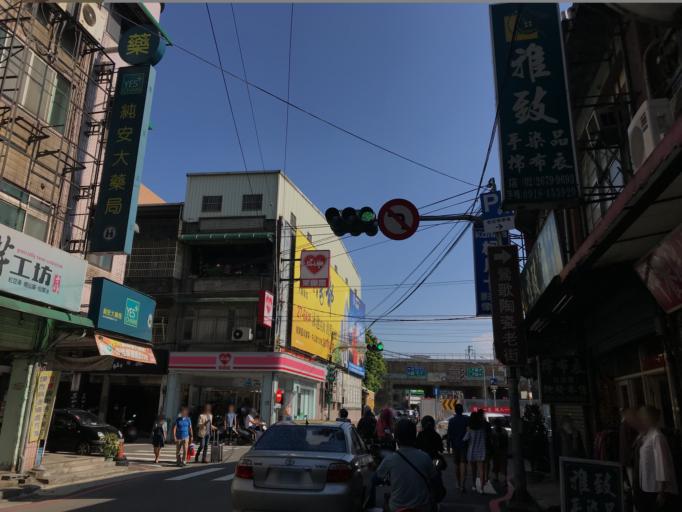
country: TW
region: Taiwan
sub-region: Taoyuan
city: Taoyuan
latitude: 24.9529
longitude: 121.3513
